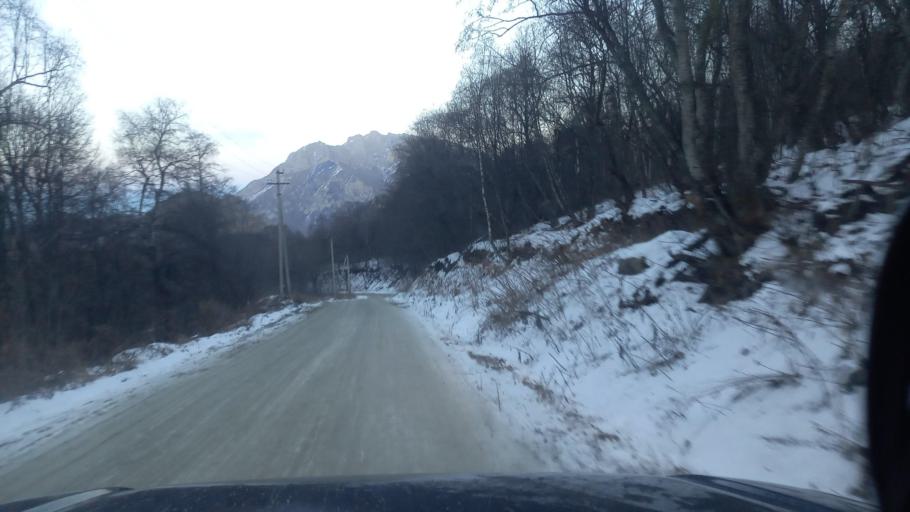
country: RU
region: Ingushetiya
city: Dzhayrakh
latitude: 42.8270
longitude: 44.5795
